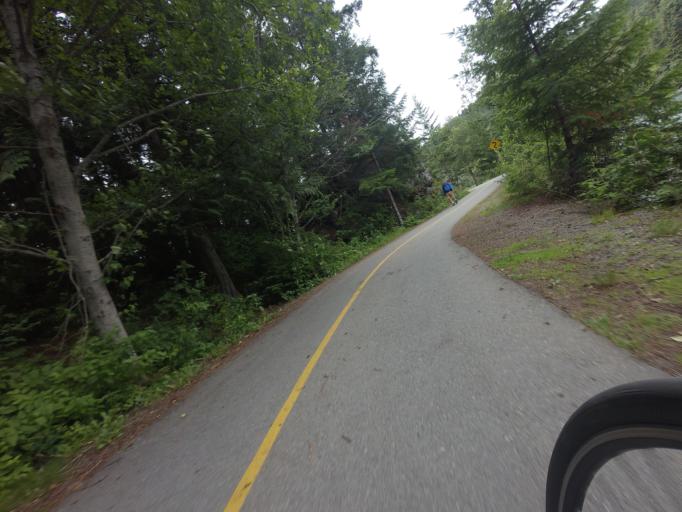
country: CA
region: British Columbia
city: Whistler
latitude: 50.1012
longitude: -122.9931
